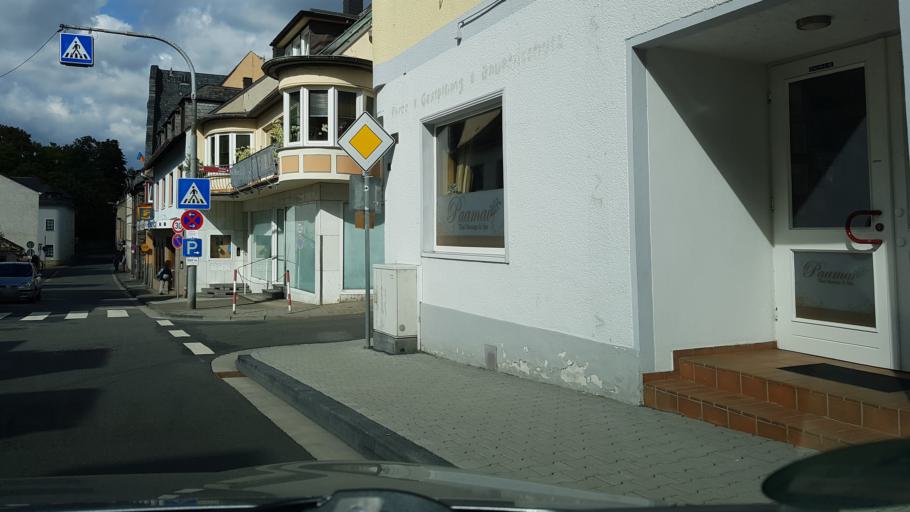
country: DE
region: Rheinland-Pfalz
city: Nassau
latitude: 50.3138
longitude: 7.8007
